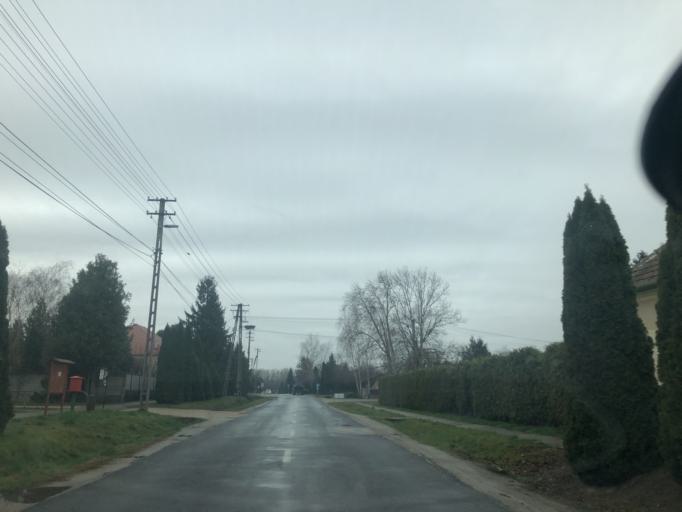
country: HU
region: Gyor-Moson-Sopron
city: Fertoszentmiklos
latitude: 47.6093
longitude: 16.9412
